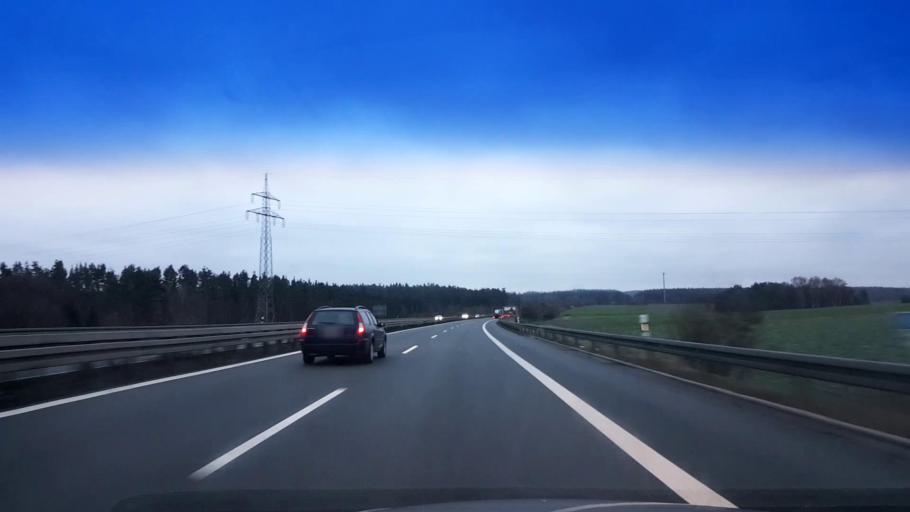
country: DE
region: Bavaria
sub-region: Upper Palatinate
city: Wiesau
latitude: 49.8906
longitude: 12.2160
